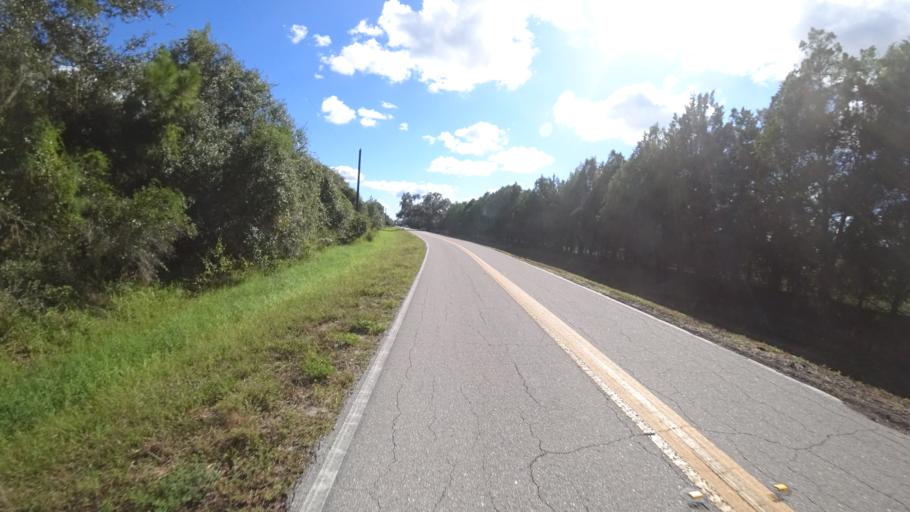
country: US
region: Florida
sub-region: Sarasota County
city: Warm Mineral Springs
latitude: 27.2585
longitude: -82.1217
